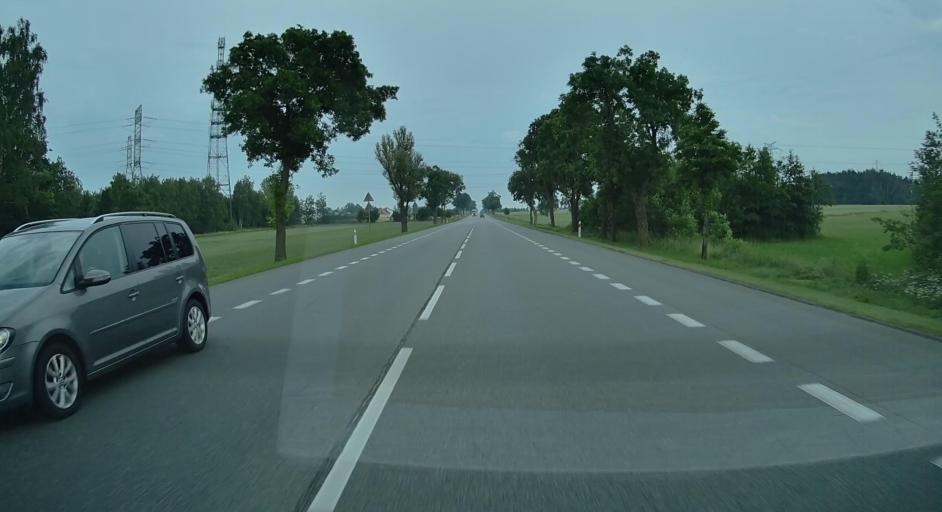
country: PL
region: Masovian Voivodeship
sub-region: Powiat siedlecki
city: Wisniew
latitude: 52.1214
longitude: 22.3549
